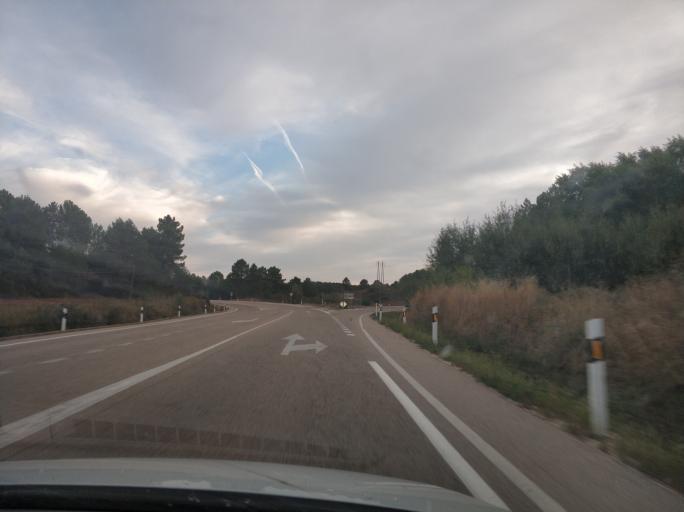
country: ES
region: Castille and Leon
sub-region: Provincia de Burgos
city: Pinilla de los Barruecos
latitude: 41.9075
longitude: -3.2764
